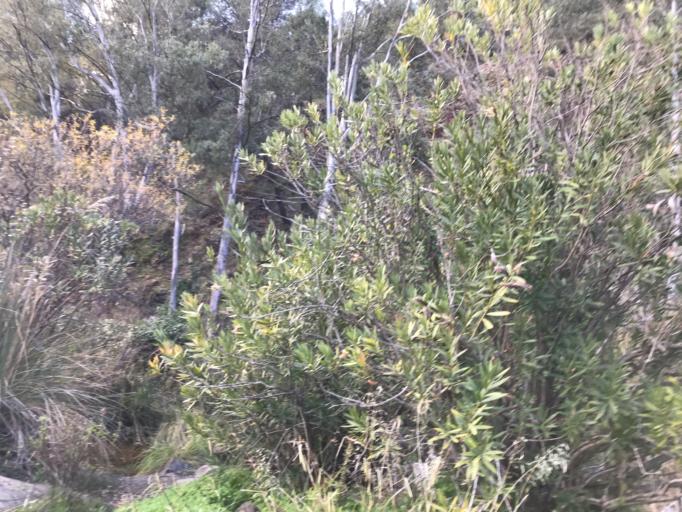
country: ES
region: Andalusia
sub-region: Provincia de Malaga
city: Tolox
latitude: 36.6787
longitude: -4.9098
